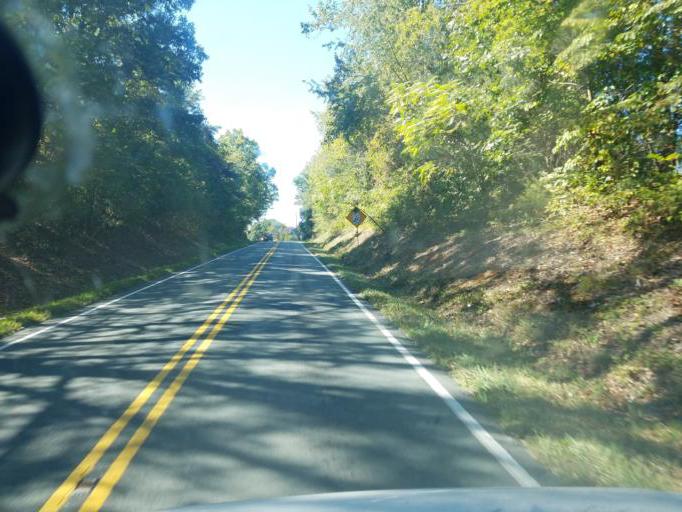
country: US
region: Virginia
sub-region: Greene County
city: Stanardsville
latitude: 38.3122
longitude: -78.4303
